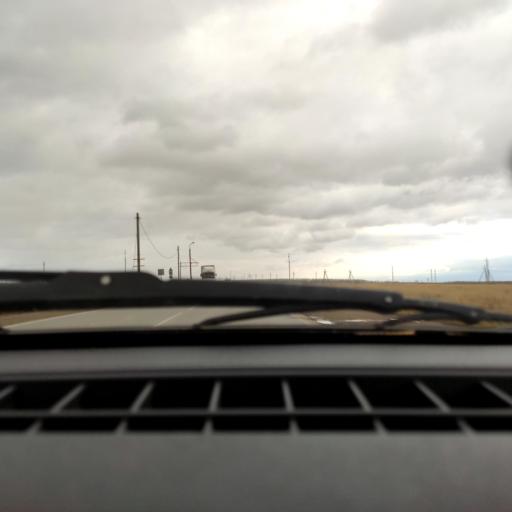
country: RU
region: Bashkortostan
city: Iglino
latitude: 54.7654
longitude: 56.2640
